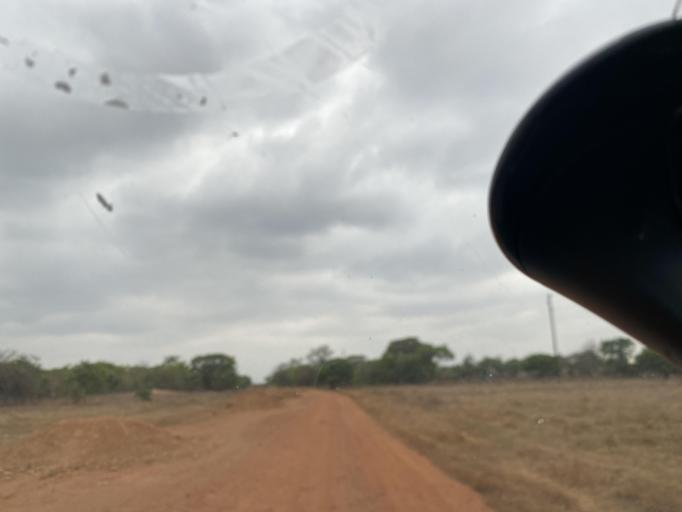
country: ZM
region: Lusaka
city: Chongwe
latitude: -15.2250
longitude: 28.7414
